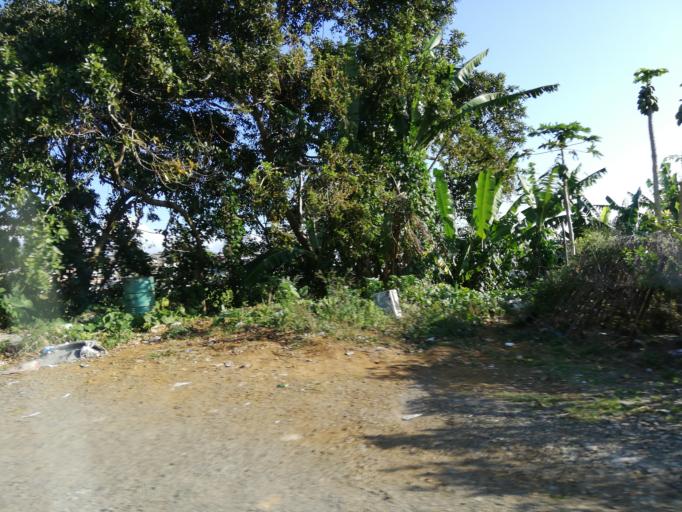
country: MU
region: Moka
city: Saint Pierre
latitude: -20.2208
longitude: 57.5274
